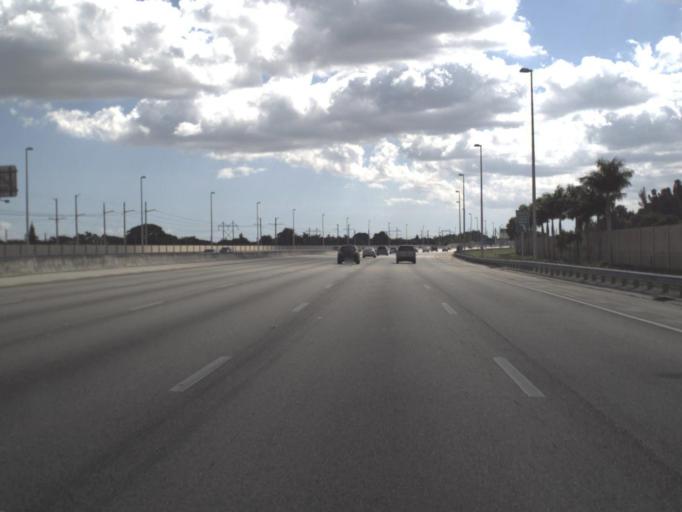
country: US
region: Florida
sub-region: Broward County
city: Lauderhill
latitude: 26.1305
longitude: -80.2182
